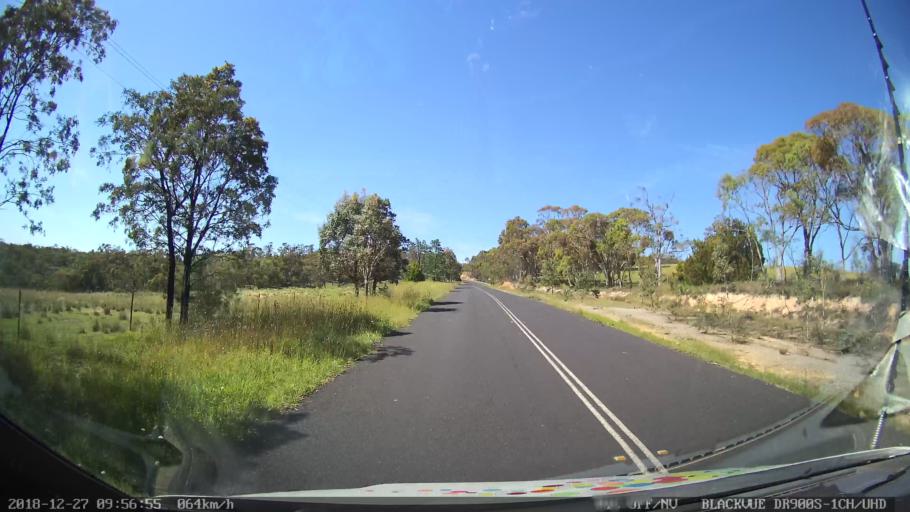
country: AU
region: New South Wales
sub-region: Lithgow
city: Portland
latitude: -33.4170
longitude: 149.9717
